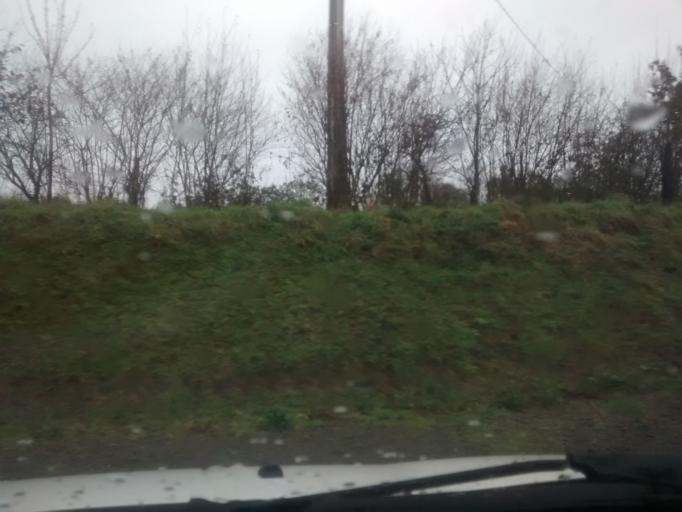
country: FR
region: Brittany
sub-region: Departement d'Ille-et-Vilaine
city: Saint-Pere
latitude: 48.5669
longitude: -1.9114
